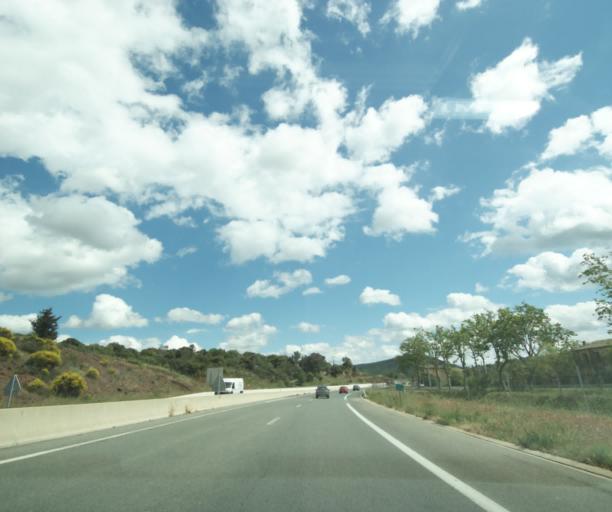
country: FR
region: Languedoc-Roussillon
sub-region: Departement de l'Herault
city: Lodeve
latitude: 43.6967
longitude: 3.3406
